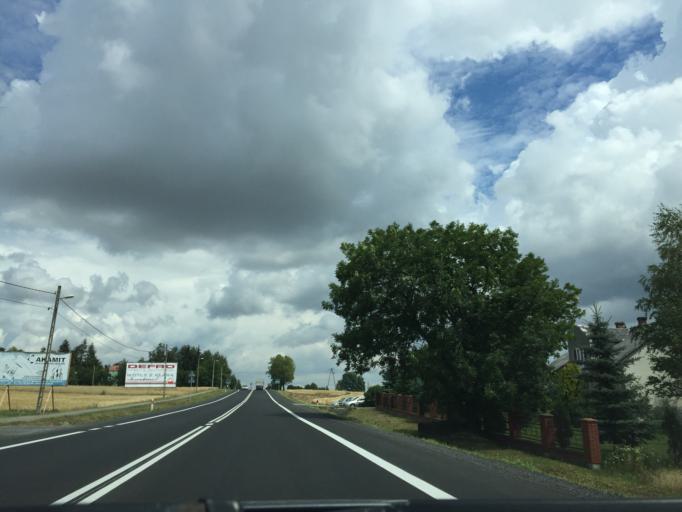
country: PL
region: Lesser Poland Voivodeship
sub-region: Powiat krakowski
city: Michalowice
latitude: 50.2053
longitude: 20.0150
